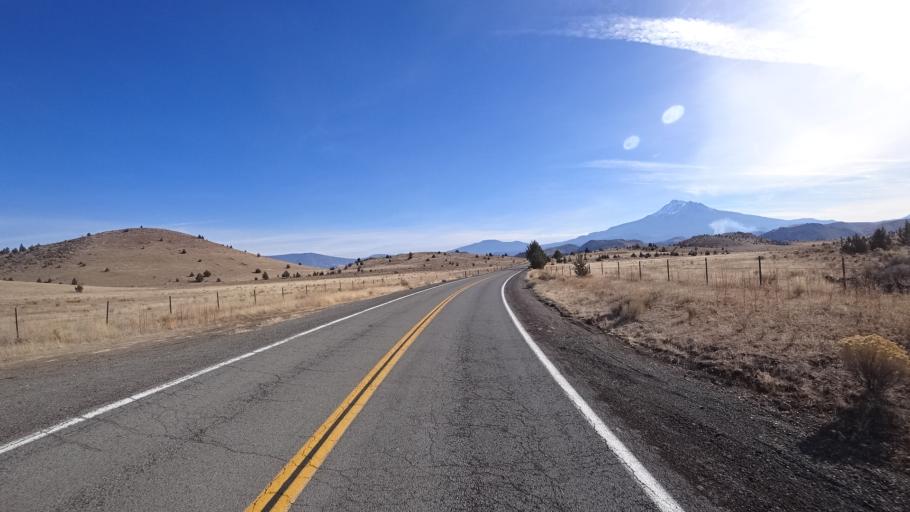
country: US
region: California
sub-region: Siskiyou County
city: Weed
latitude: 41.5540
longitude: -122.4804
